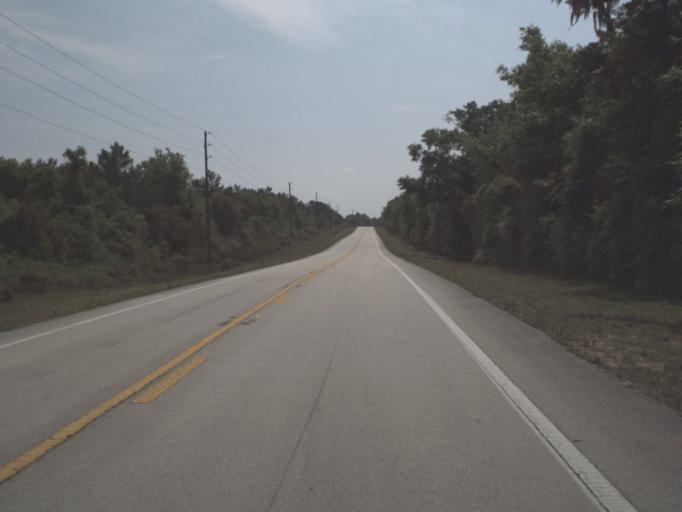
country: US
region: Florida
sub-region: Lake County
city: Astor
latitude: 29.2975
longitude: -81.6643
